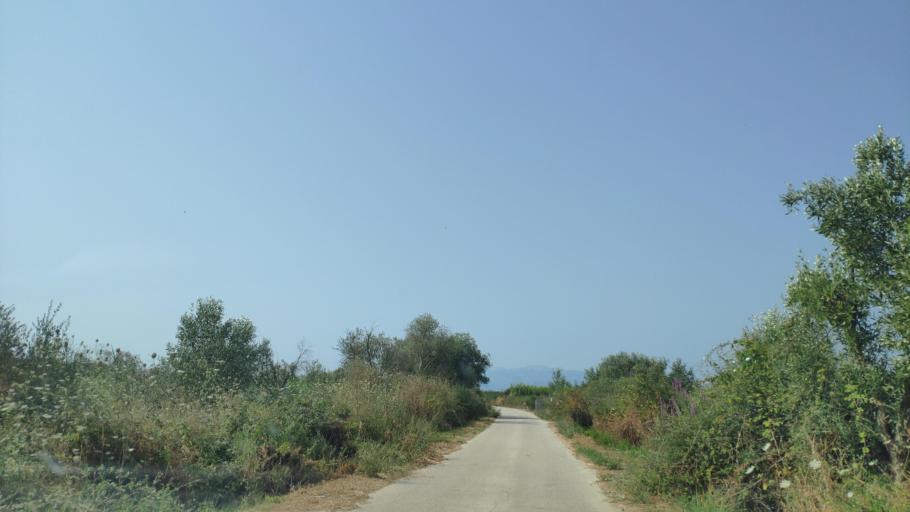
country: GR
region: Epirus
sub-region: Nomos Artas
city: Kompoti
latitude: 39.0575
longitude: 21.0722
